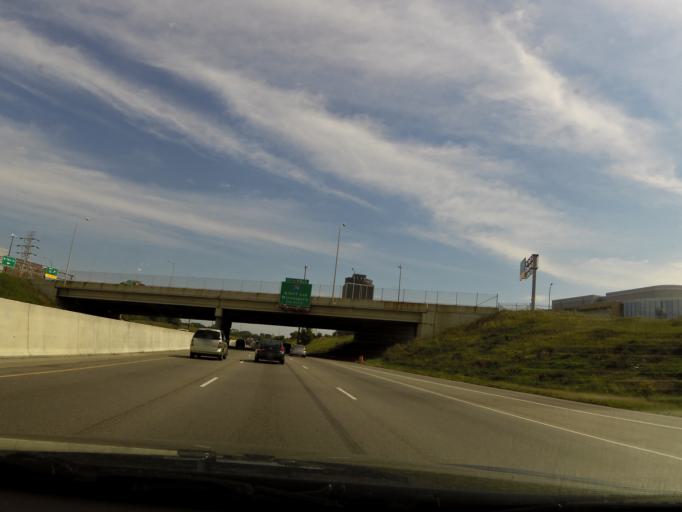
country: US
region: Minnesota
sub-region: Hennepin County
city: Edina
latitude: 44.8587
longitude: -93.3305
